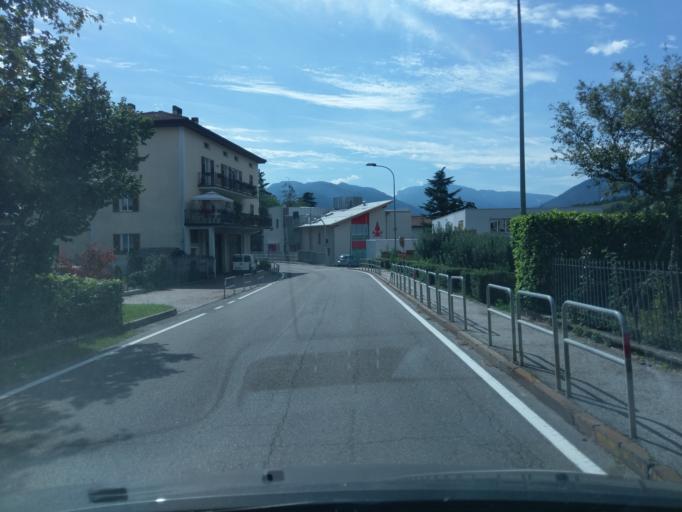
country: IT
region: Trentino-Alto Adige
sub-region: Provincia di Trento
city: Denno
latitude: 46.2744
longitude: 11.0482
